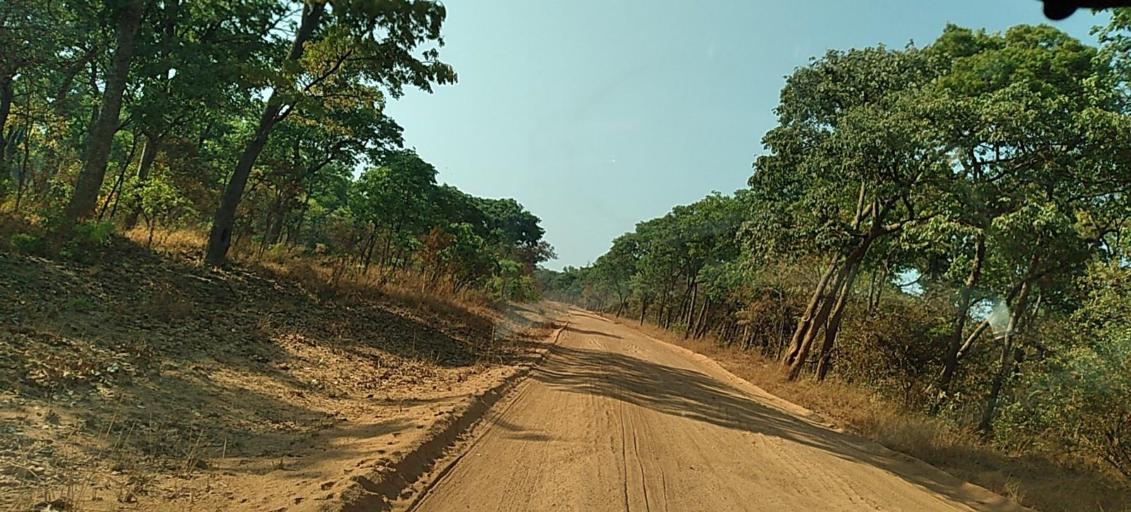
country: ZM
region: North-Western
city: Kasempa
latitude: -13.6617
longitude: 26.0102
